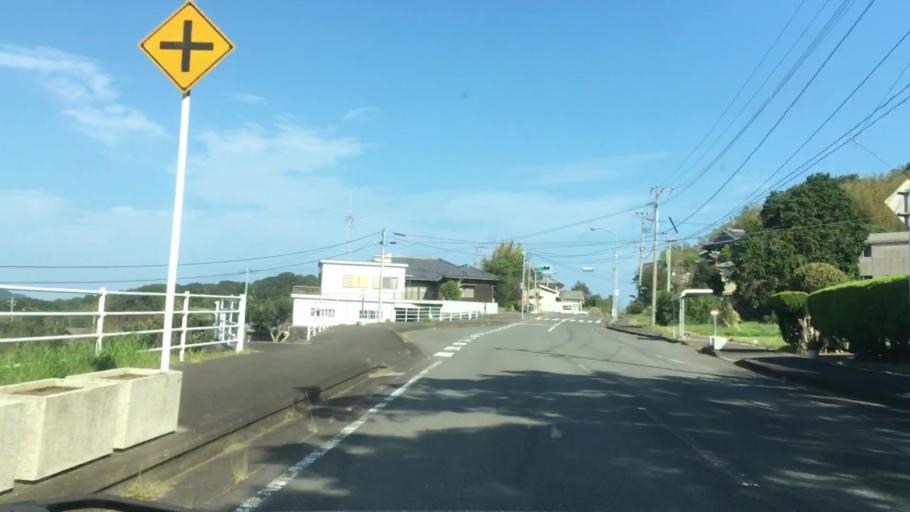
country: JP
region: Nagasaki
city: Sasebo
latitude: 33.0146
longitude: 129.6549
